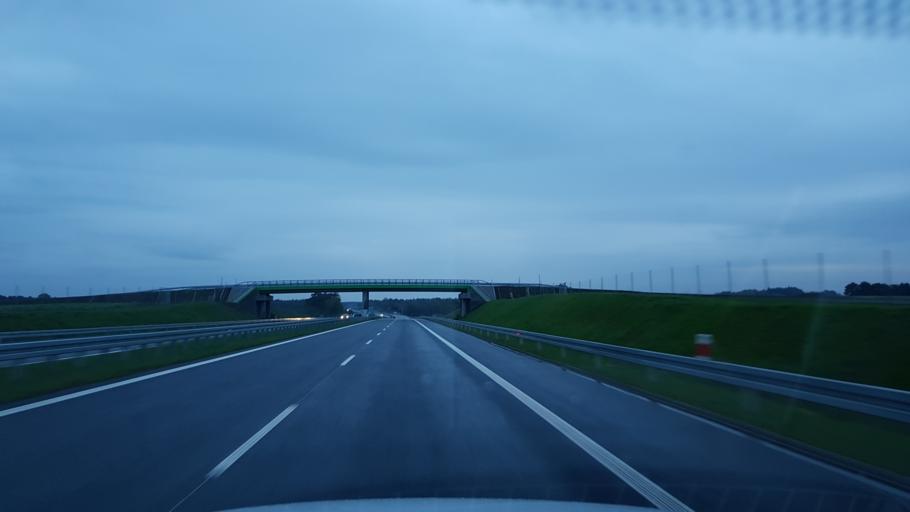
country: PL
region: West Pomeranian Voivodeship
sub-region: Powiat gryficki
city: Brojce
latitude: 53.9240
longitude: 15.3867
